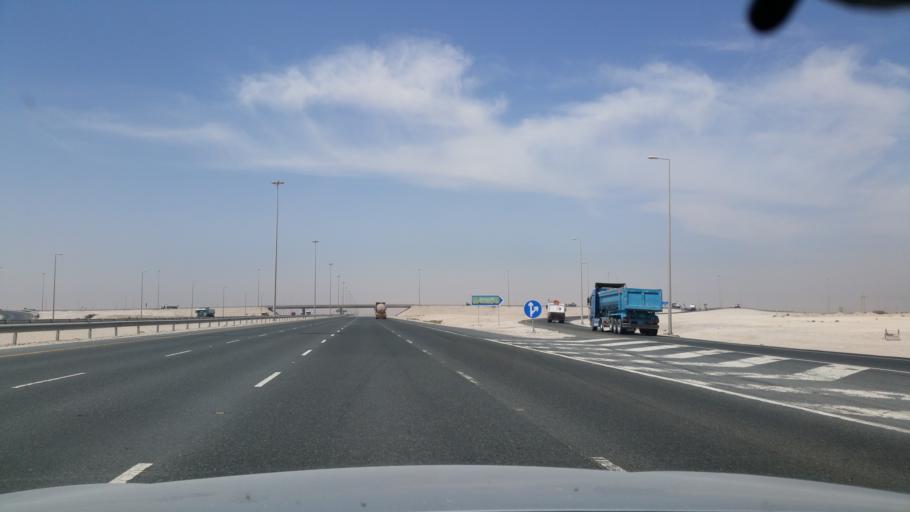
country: QA
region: Baladiyat ar Rayyan
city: Ash Shahaniyah
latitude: 25.1119
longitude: 51.1726
